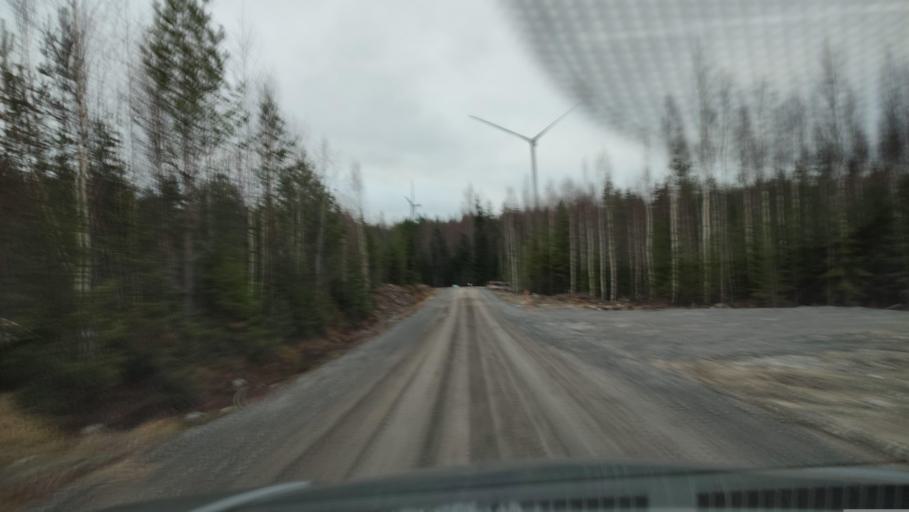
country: FI
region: Southern Ostrobothnia
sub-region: Suupohja
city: Karijoki
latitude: 62.2077
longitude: 21.5997
